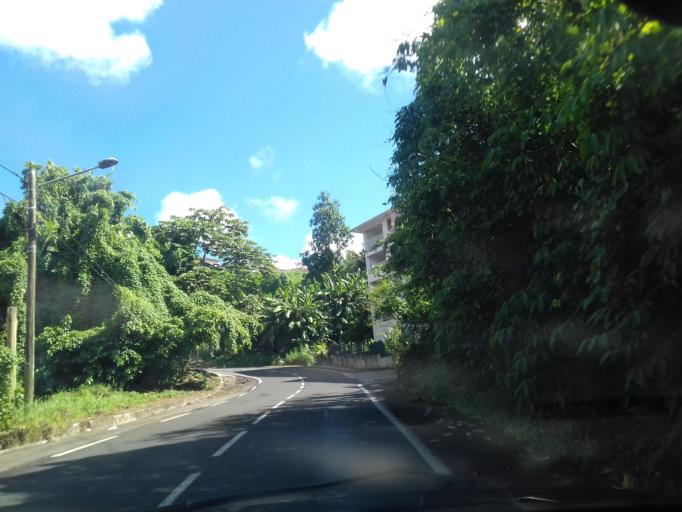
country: MQ
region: Martinique
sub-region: Martinique
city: Le Gros-Morne
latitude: 14.7135
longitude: -61.0132
